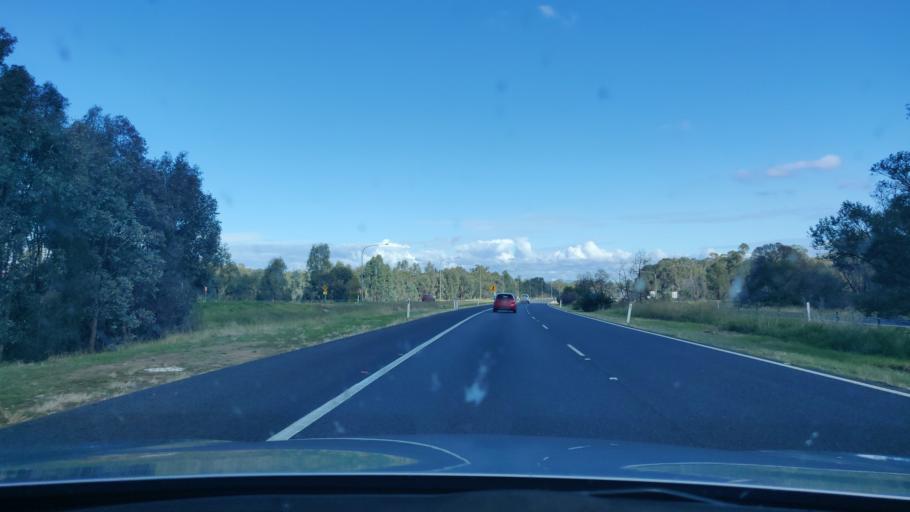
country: AU
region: New South Wales
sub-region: Albury Municipality
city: Lavington
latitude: -36.0408
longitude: 146.9730
